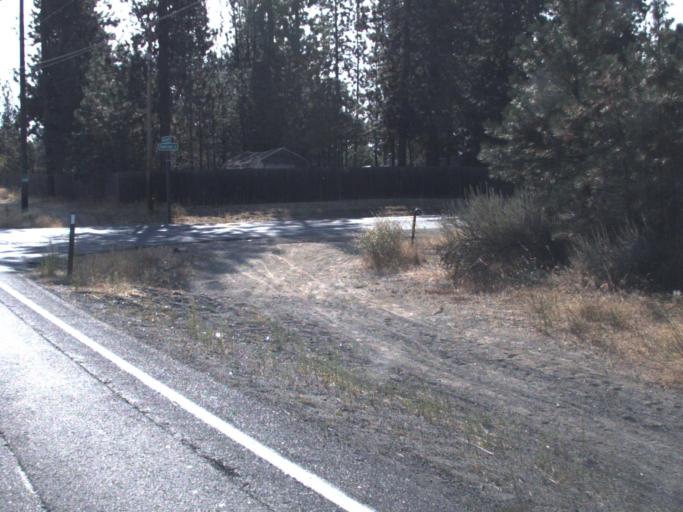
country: US
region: Washington
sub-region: Spokane County
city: Fairwood
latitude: 47.8126
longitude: -117.5694
